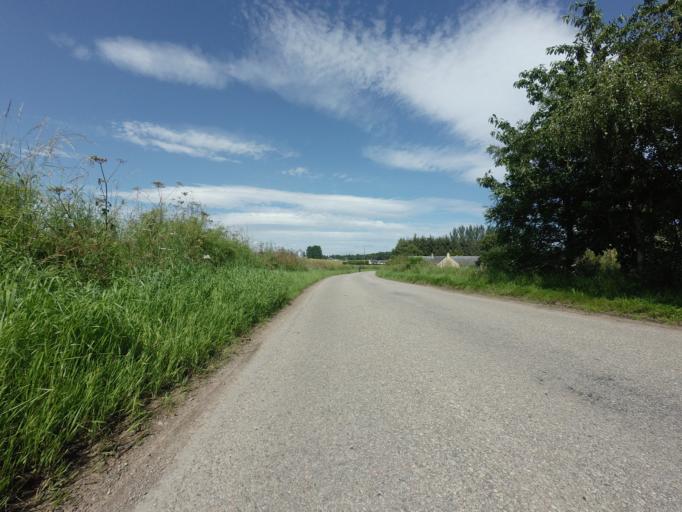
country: GB
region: Scotland
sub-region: Highland
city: Inverness
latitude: 57.5268
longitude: -4.3180
